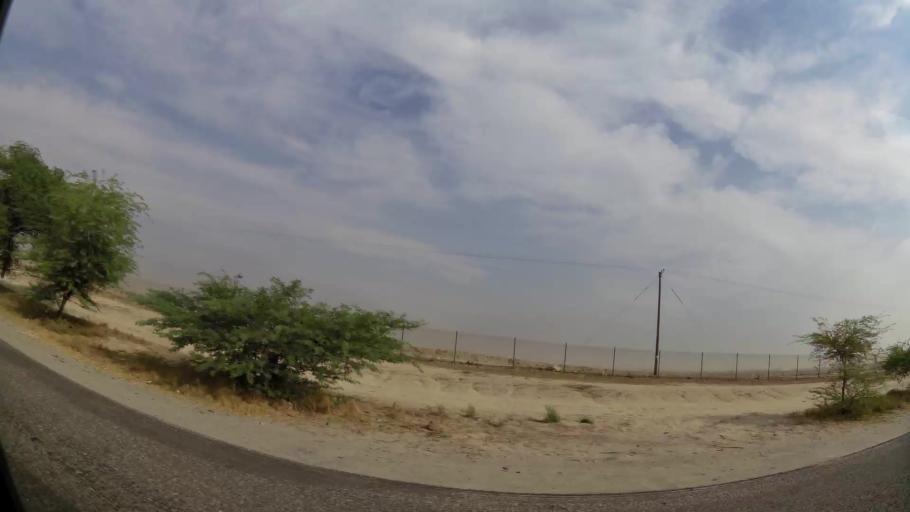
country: KW
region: Muhafazat al Jahra'
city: Al Jahra'
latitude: 29.2900
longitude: 47.7637
